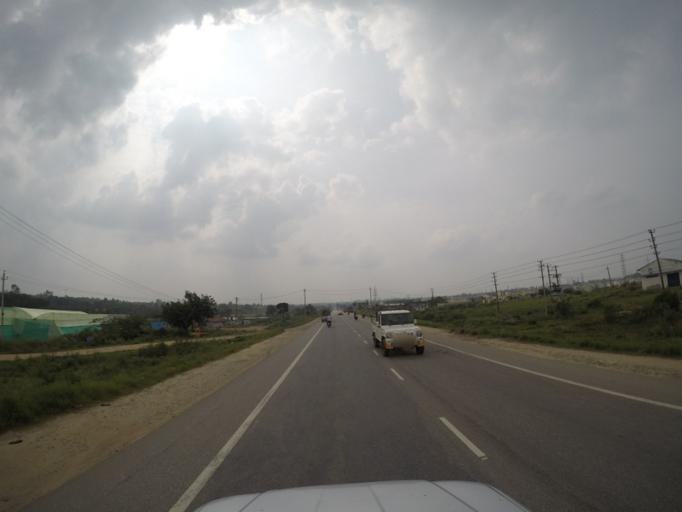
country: IN
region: Karnataka
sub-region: Hassan
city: Hassan
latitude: 12.9888
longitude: 76.0997
